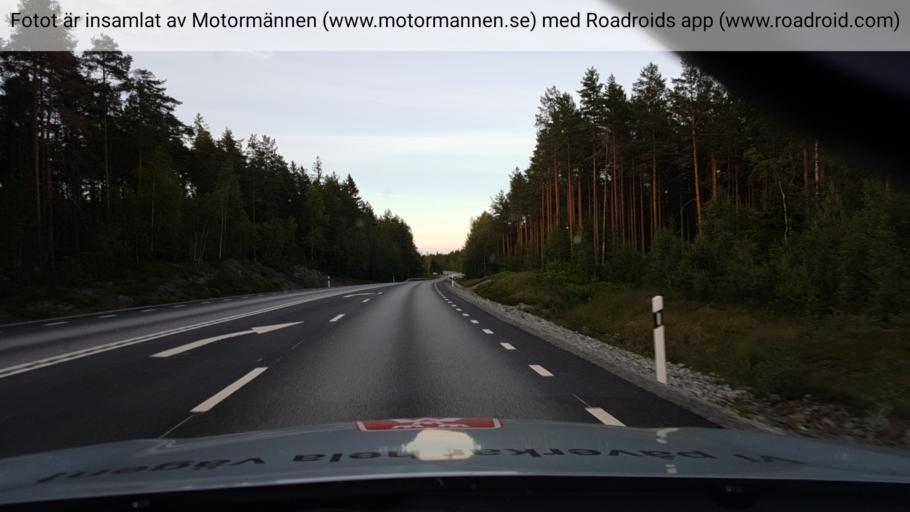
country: SE
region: Vaestmanland
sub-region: Skinnskattebergs Kommun
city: Skinnskatteberg
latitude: 59.8306
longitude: 15.5419
